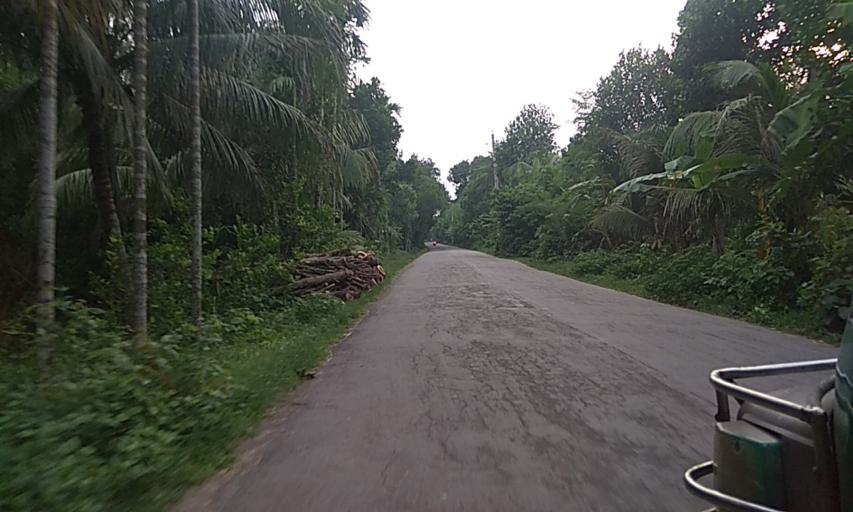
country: BD
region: Dhaka
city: Dohar
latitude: 23.4610
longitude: 89.9917
